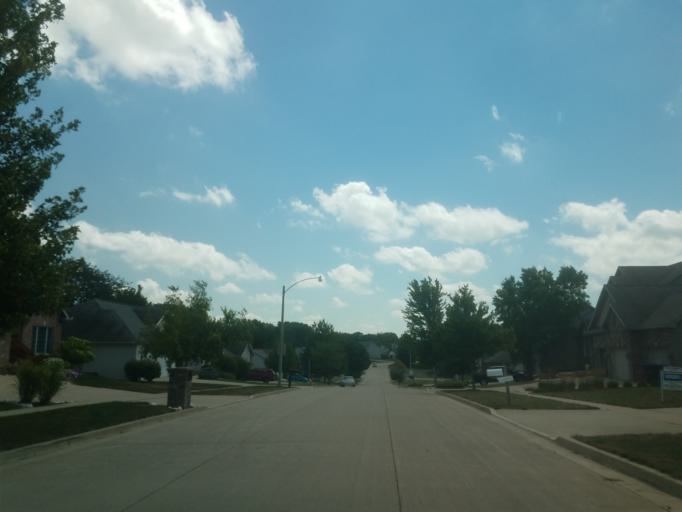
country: US
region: Illinois
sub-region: McLean County
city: Bloomington
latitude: 40.4552
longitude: -89.0330
